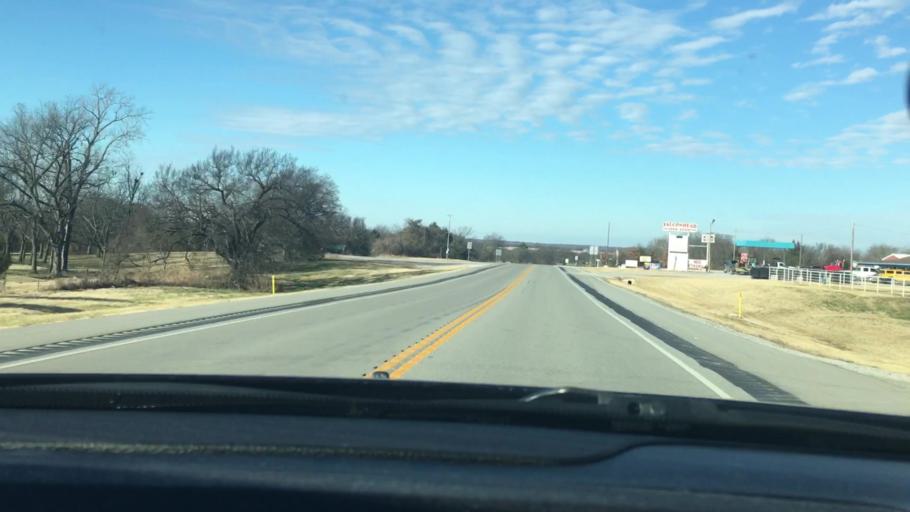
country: US
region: Oklahoma
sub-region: Love County
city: Marietta
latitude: 33.9407
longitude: -97.2803
